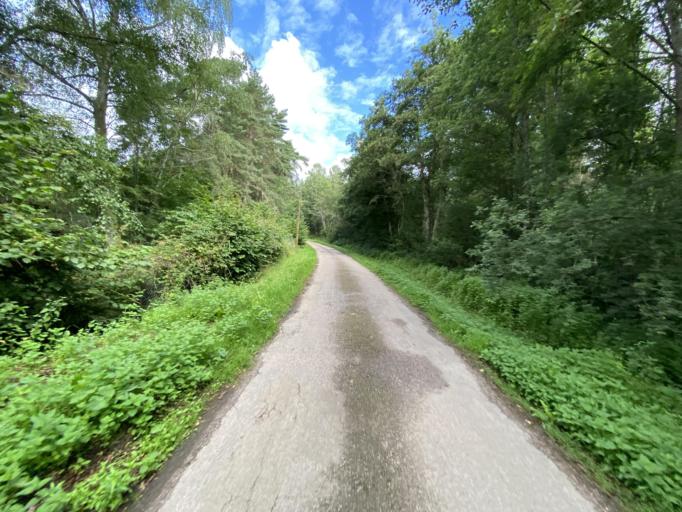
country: FR
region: Bourgogne
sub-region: Departement de la Cote-d'Or
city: Saulieu
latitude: 47.2858
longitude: 4.1731
